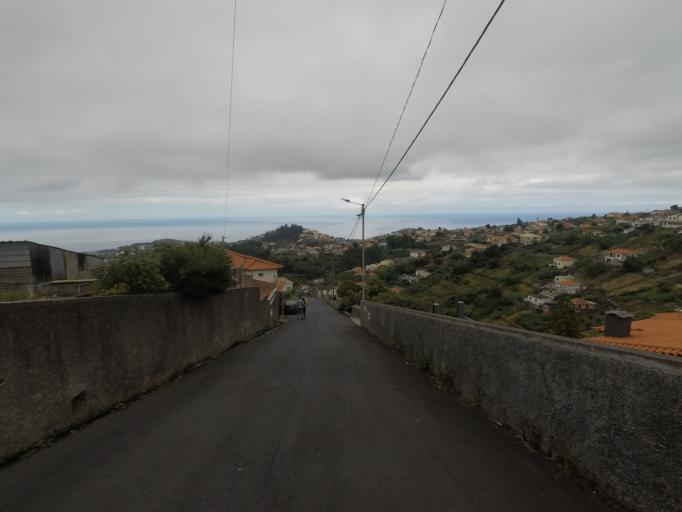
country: PT
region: Madeira
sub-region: Funchal
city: Nossa Senhora do Monte
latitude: 32.6774
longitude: -16.9432
